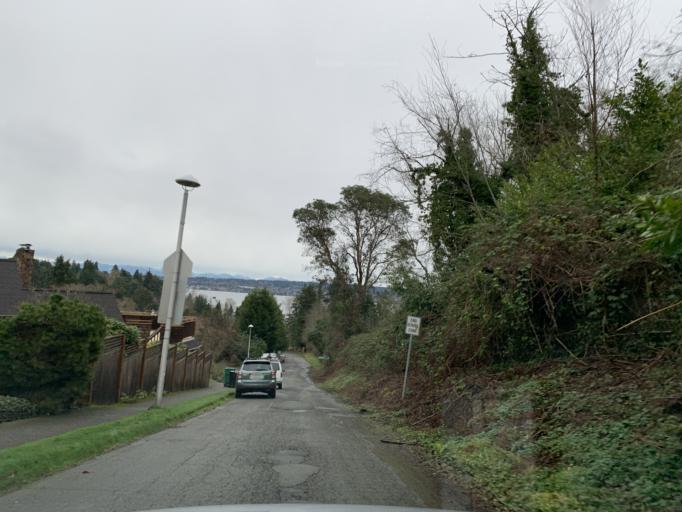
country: US
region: Washington
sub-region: King County
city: Yarrow Point
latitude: 47.6649
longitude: -122.2718
